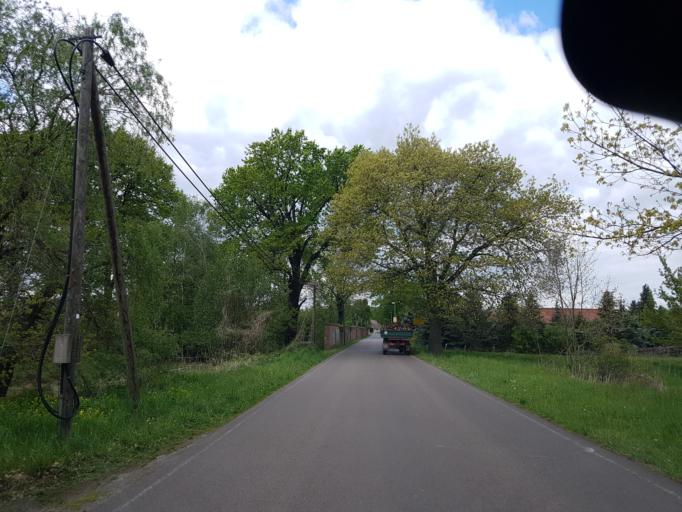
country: DE
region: Brandenburg
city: Altdobern
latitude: 51.6573
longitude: 14.0178
